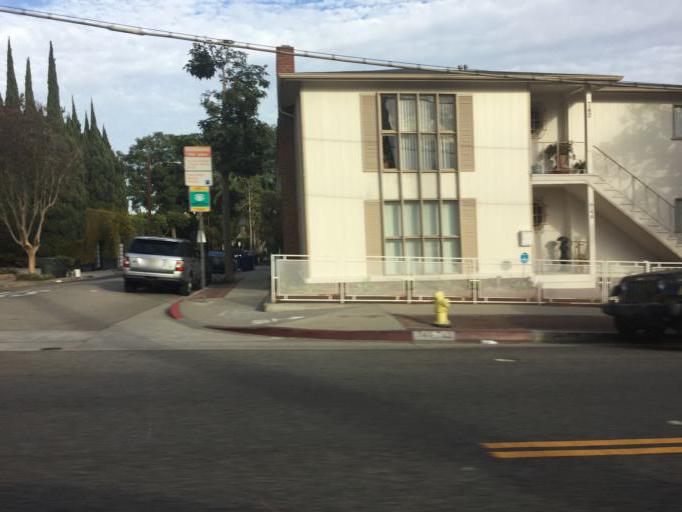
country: US
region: California
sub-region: Los Angeles County
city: Beverly Hills
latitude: 34.0843
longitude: -118.3898
